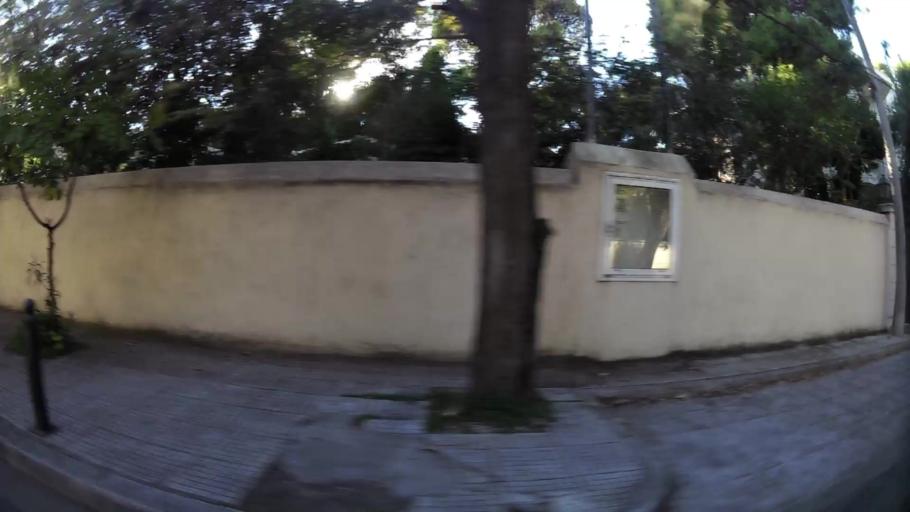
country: GR
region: Attica
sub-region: Nomarchia Athinas
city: Kifisia
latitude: 38.0811
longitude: 23.8108
